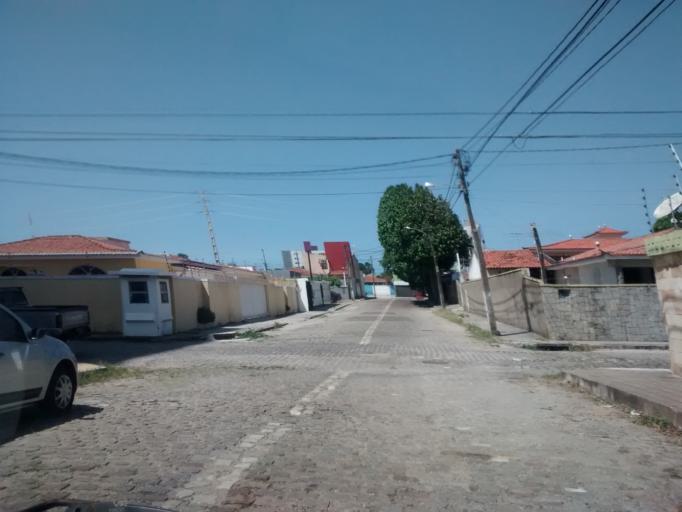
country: BR
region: Rio Grande do Norte
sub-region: Natal
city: Natal
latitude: -5.8187
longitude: -35.2174
